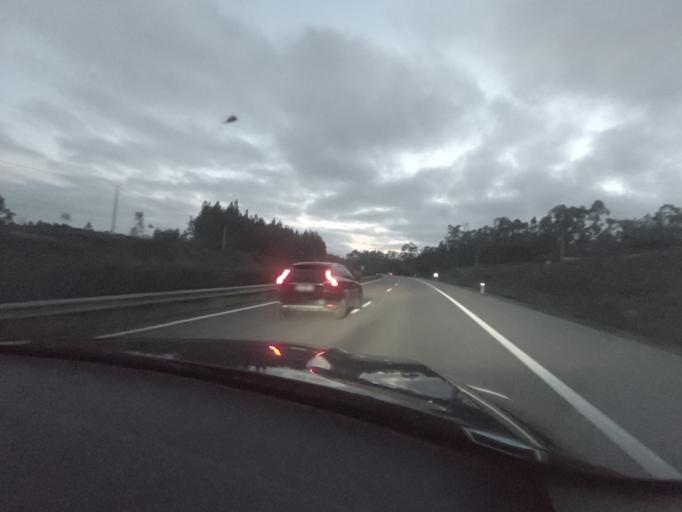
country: PT
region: Leiria
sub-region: Pombal
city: Pombal
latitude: 39.9579
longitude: -8.6667
